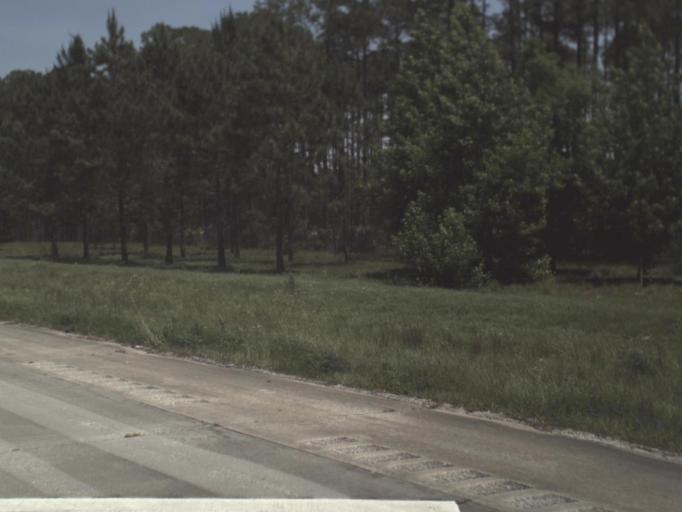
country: US
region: Florida
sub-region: Saint Johns County
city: Palm Valley
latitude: 30.1963
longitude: -81.5136
